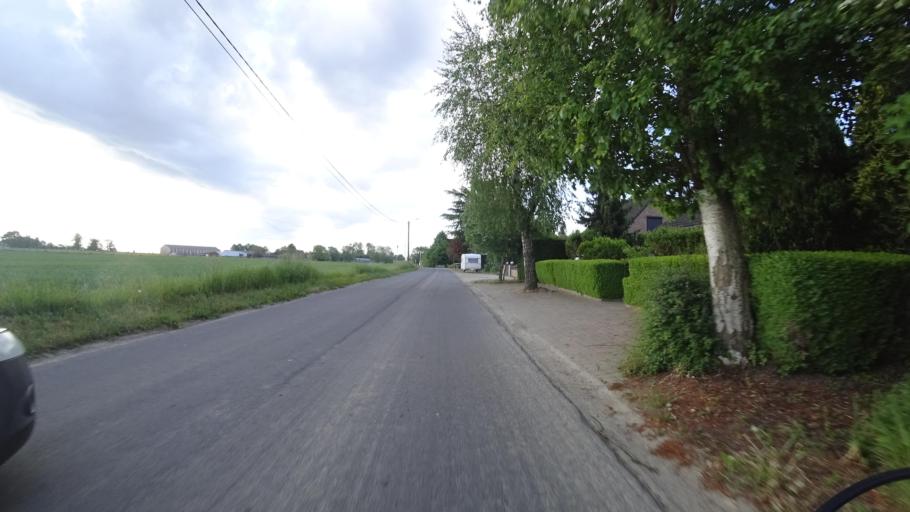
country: BE
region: Wallonia
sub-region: Province de Namur
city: Gembloux
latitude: 50.5356
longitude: 4.7497
